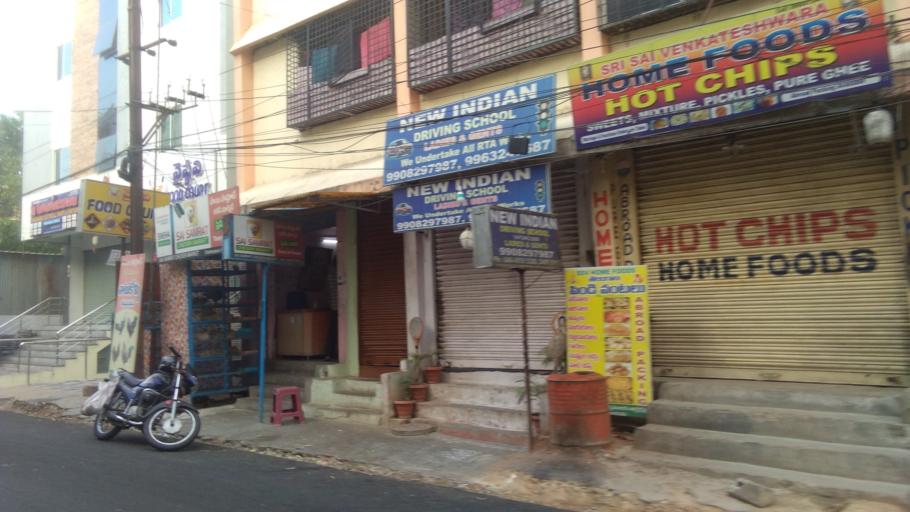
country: IN
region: Telangana
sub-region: Rangareddi
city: Gaddi Annaram
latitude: 17.3712
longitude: 78.5321
